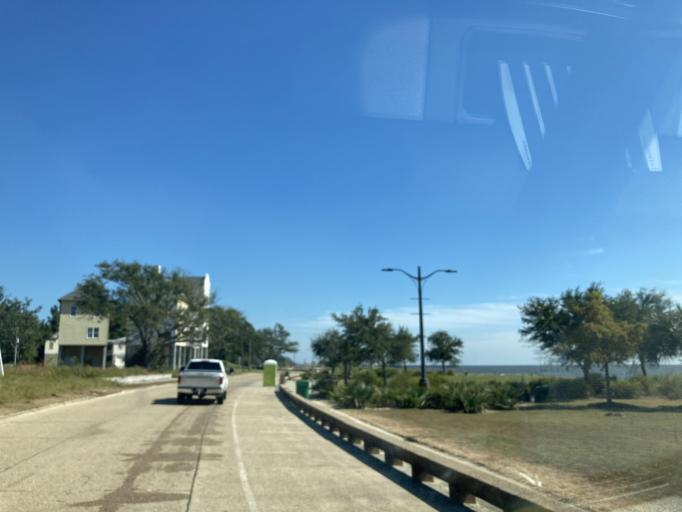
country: US
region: Mississippi
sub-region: Jackson County
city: Ocean Springs
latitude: 30.4080
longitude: -88.8348
